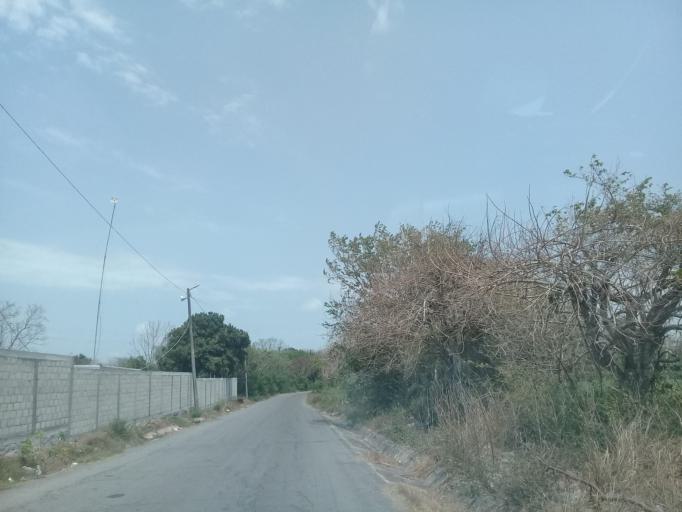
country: MX
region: Veracruz
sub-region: Veracruz
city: Delfino Victoria (Santa Fe)
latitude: 19.1697
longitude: -96.2885
